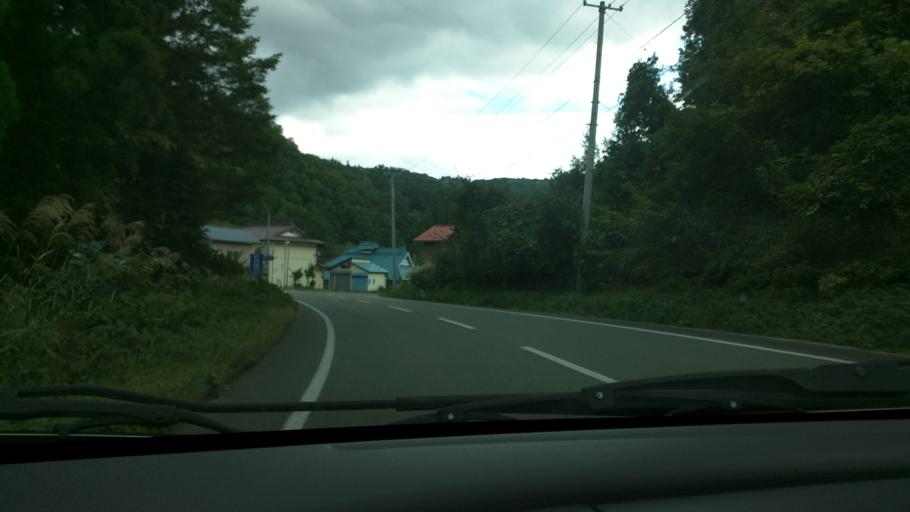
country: JP
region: Fukushima
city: Kitakata
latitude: 37.4655
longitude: 139.6969
